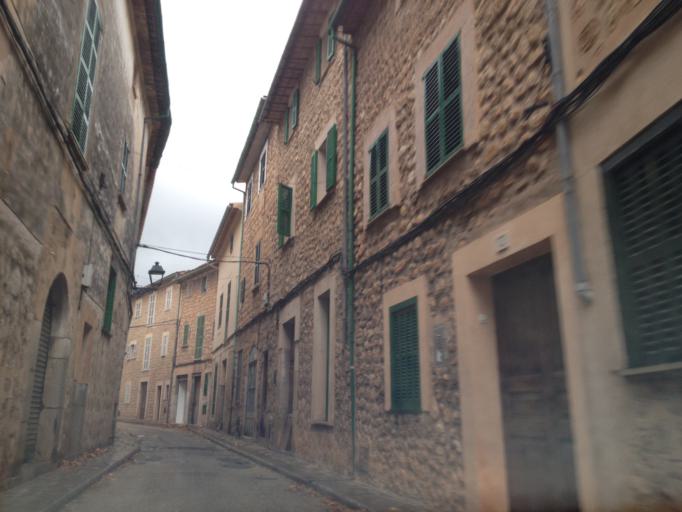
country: ES
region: Balearic Islands
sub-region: Illes Balears
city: Soller
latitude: 39.7693
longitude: 2.7161
